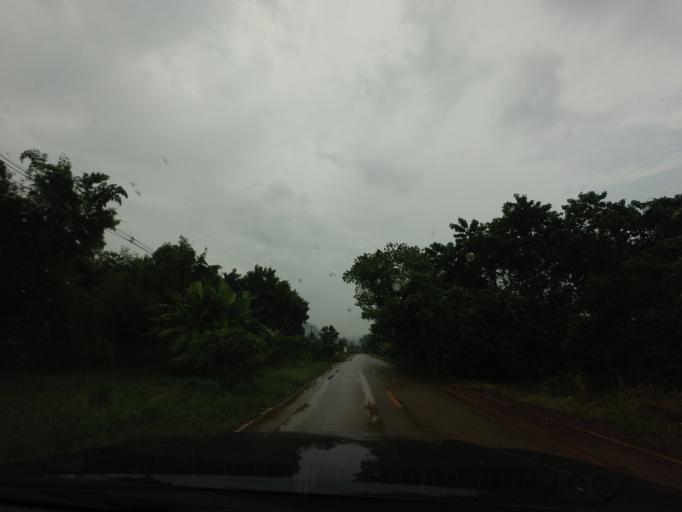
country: TH
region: Nong Khai
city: Sangkhom
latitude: 18.2052
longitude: 102.0683
